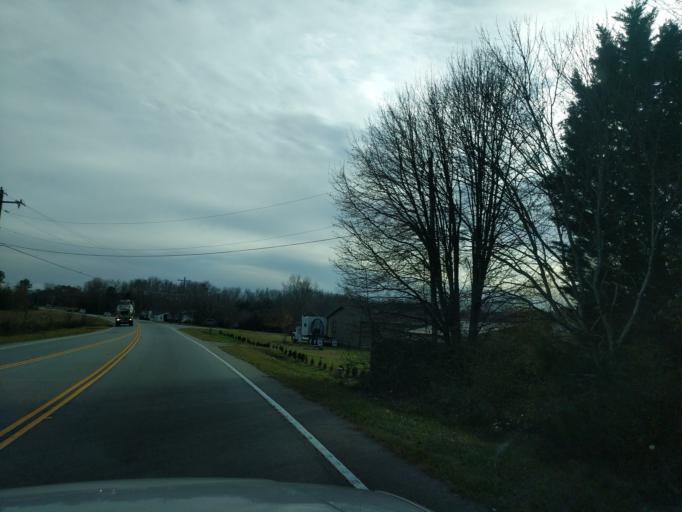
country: US
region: South Carolina
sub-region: Anderson County
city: Piedmont
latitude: 34.7165
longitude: -82.5632
